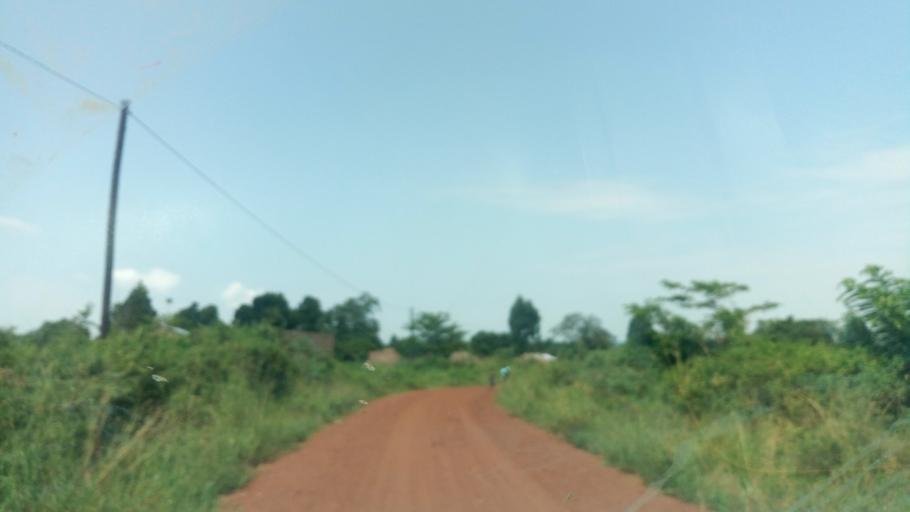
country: UG
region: Western Region
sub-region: Masindi District
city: Masindi
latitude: 1.6847
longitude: 31.8350
